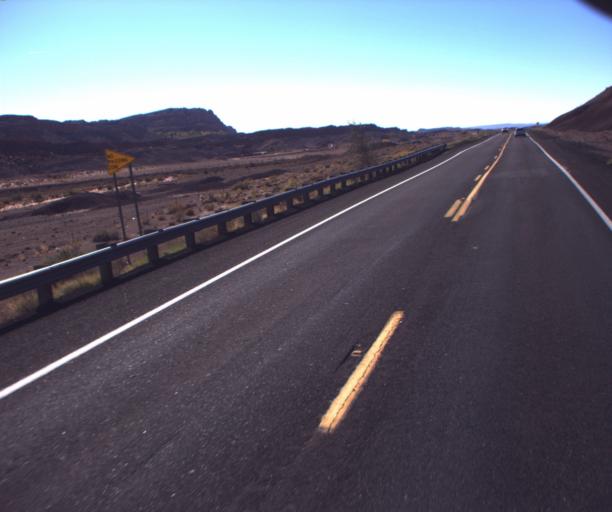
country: US
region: Arizona
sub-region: Coconino County
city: Tuba City
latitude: 36.1979
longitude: -111.3933
